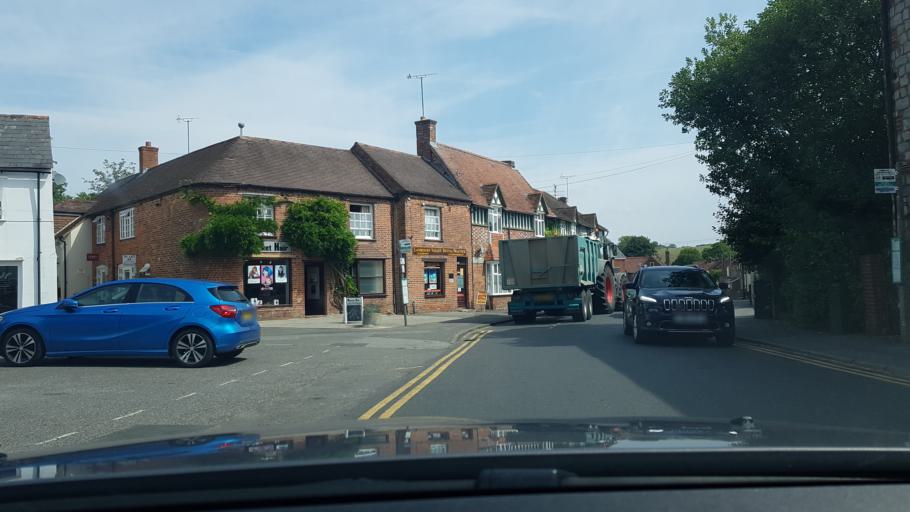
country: GB
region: England
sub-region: West Berkshire
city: Lambourn
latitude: 51.5082
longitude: -1.5310
